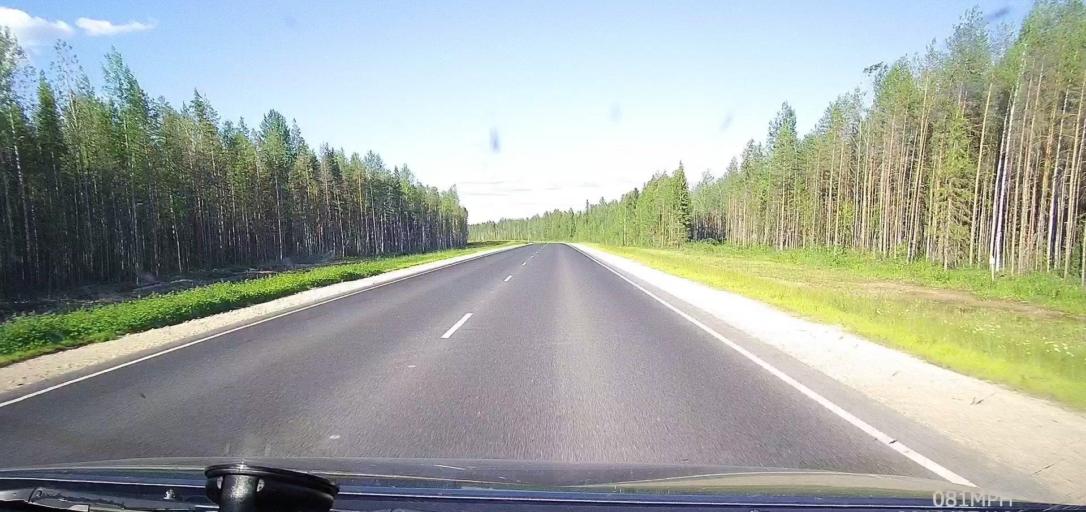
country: RU
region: Arkhangelskaya
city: Yemtsa
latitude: 63.1525
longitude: 40.5117
